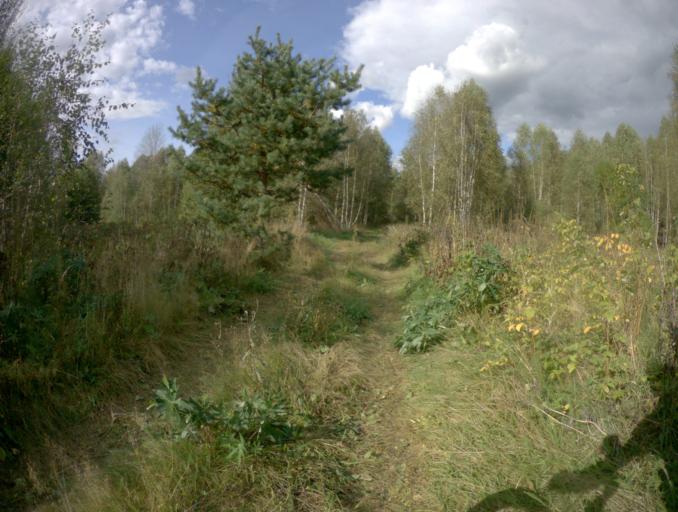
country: RU
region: Vladimir
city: Ivanishchi
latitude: 55.8492
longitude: 40.3968
